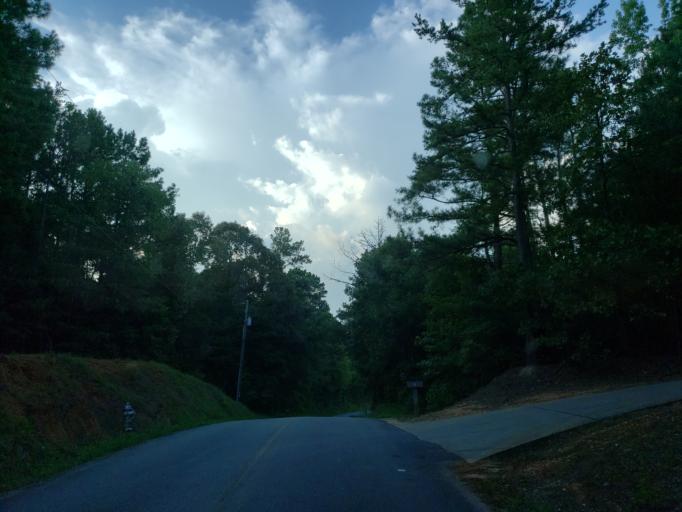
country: US
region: Georgia
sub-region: Bartow County
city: Euharlee
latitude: 34.0778
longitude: -84.9434
